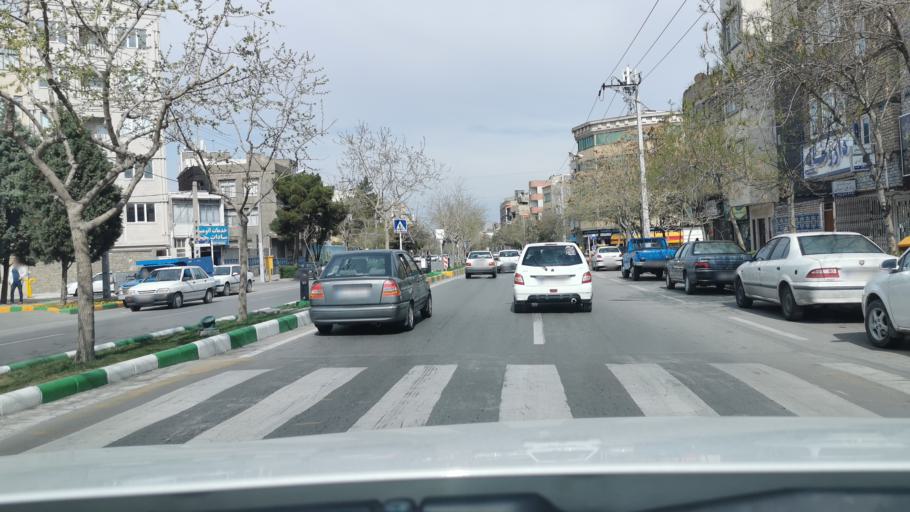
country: IR
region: Razavi Khorasan
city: Mashhad
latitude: 36.3176
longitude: 59.5998
